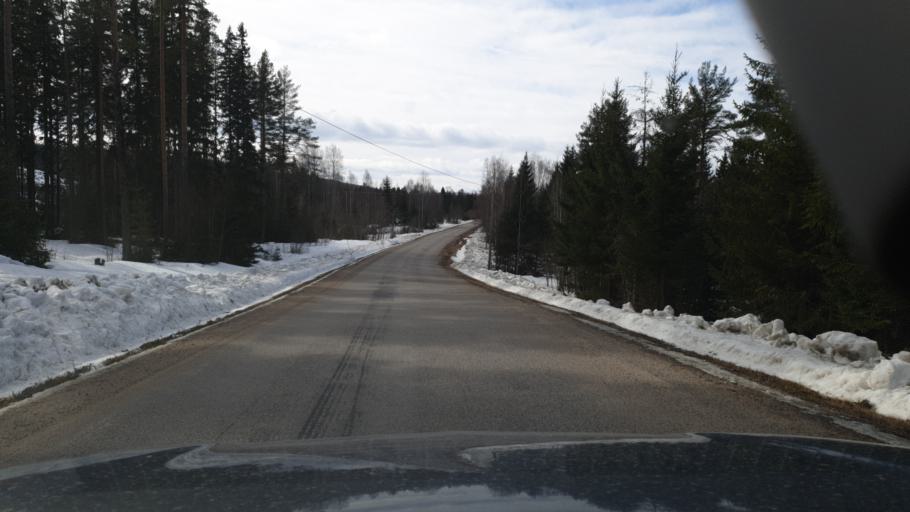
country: SE
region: Gaevleborg
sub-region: Ljusdals Kommun
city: Farila
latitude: 61.8420
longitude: 15.8759
